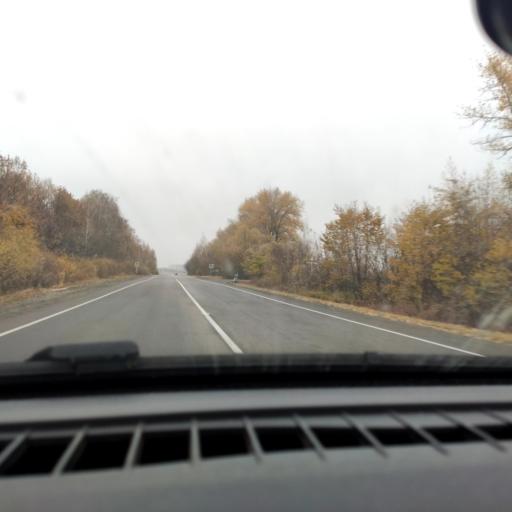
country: RU
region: Voronezj
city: Kolodeznyy
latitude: 51.3598
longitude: 39.0236
